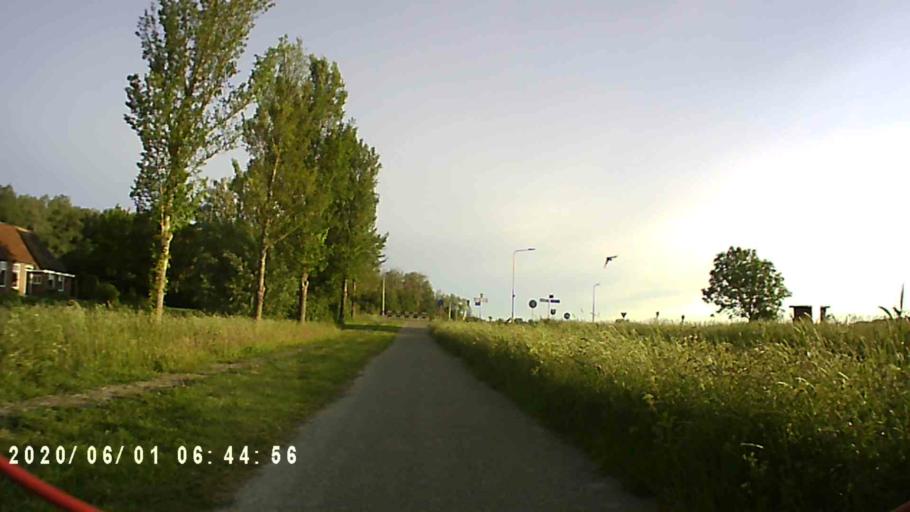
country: NL
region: Friesland
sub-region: Gemeente Kollumerland en Nieuwkruisland
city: Kollum
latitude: 53.3026
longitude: 6.1474
